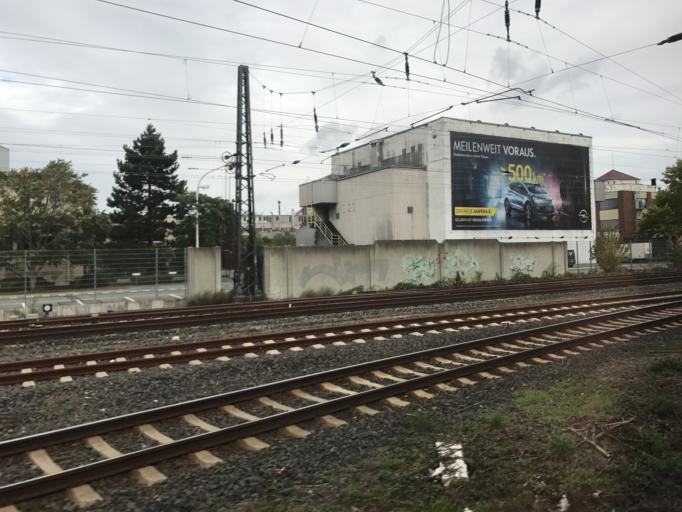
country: DE
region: Hesse
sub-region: Regierungsbezirk Darmstadt
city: Russelsheim
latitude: 49.9902
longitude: 8.4085
